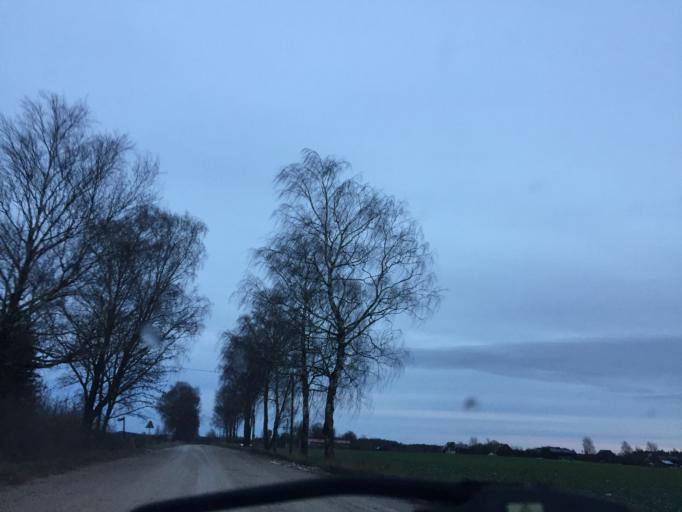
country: LV
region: Burtnieki
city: Matisi
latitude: 57.6276
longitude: 25.1981
